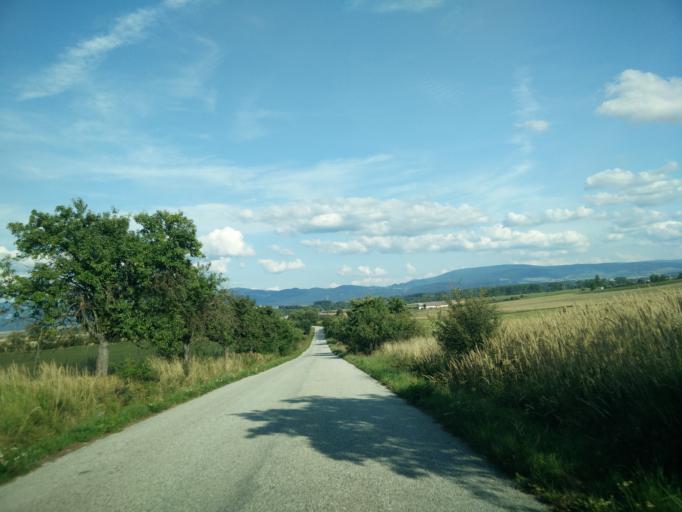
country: SK
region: Nitriansky
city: Handlova
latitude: 48.8902
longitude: 18.7541
